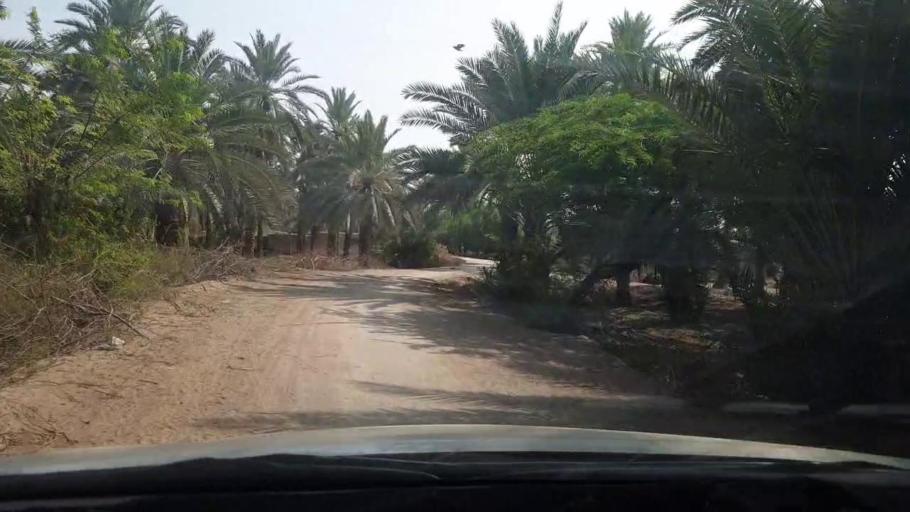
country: PK
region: Sindh
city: Rohri
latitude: 27.6012
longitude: 68.8901
